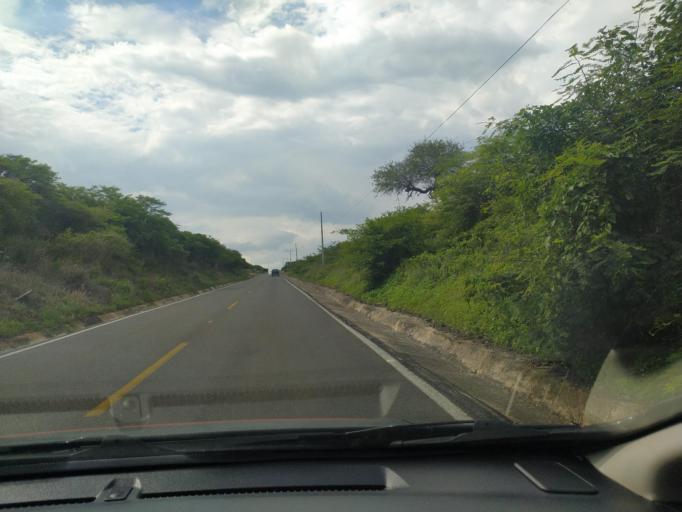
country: MX
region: Jalisco
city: Villa Corona
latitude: 20.3738
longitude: -103.6701
